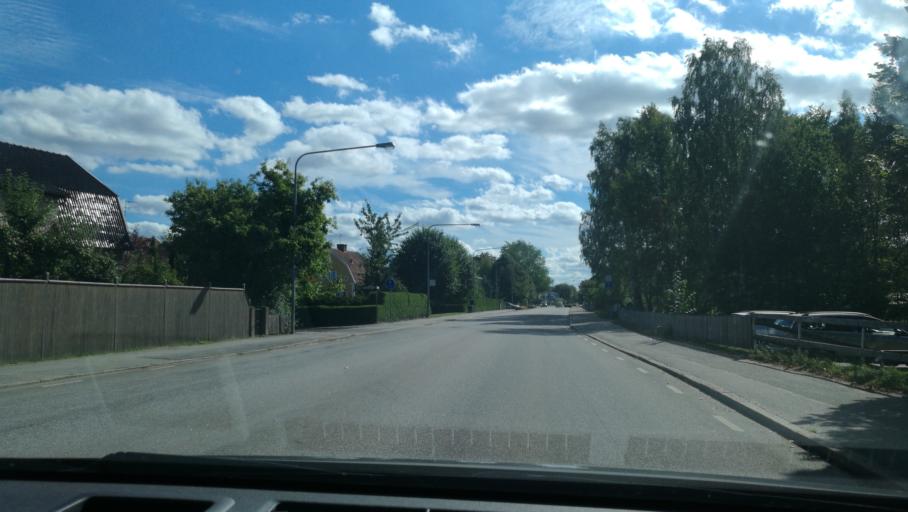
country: SE
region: Vaestra Goetaland
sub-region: Mariestads Kommun
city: Mariestad
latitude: 58.6988
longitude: 13.8367
